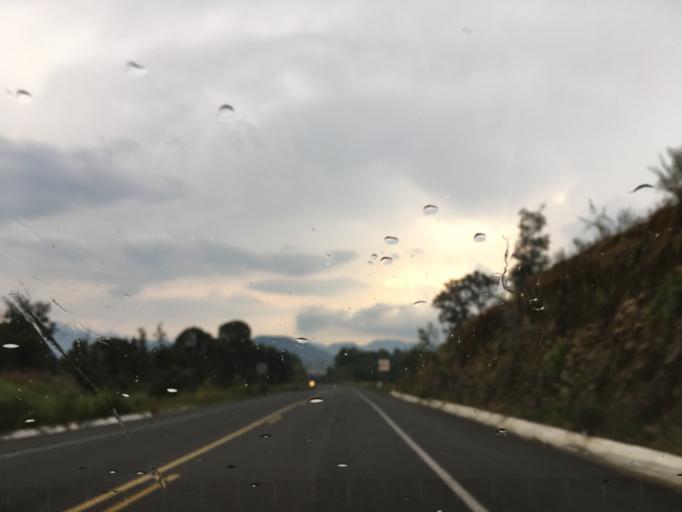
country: MX
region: Michoacan
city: Nuevo San Juan Parangaricutiro
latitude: 19.5050
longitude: -102.1412
